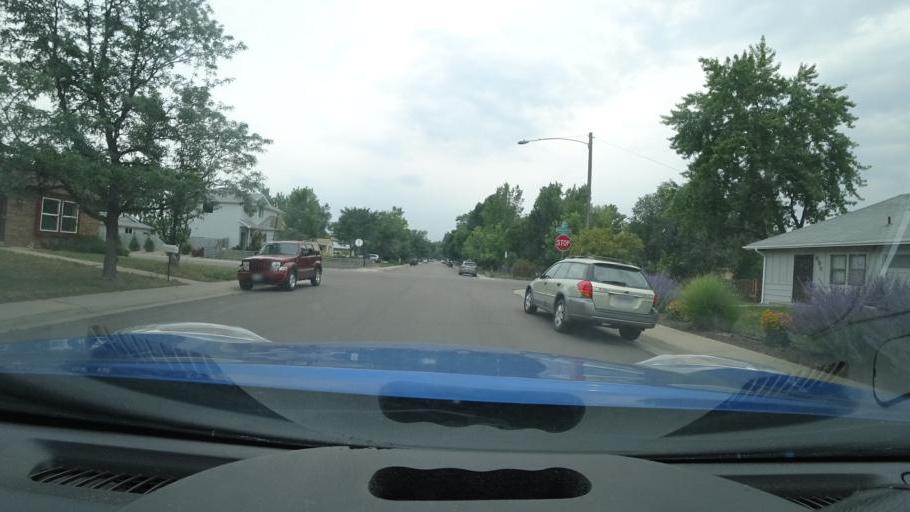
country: US
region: Colorado
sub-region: Arapahoe County
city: Glendale
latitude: 39.7006
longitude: -104.9152
